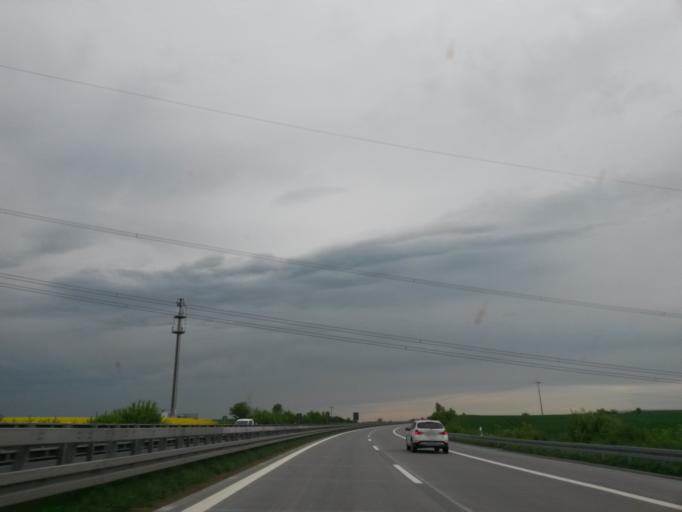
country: DE
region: Baden-Wuerttemberg
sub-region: Regierungsbezirk Stuttgart
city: Tauberbischofsheim
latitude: 49.5749
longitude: 9.6423
